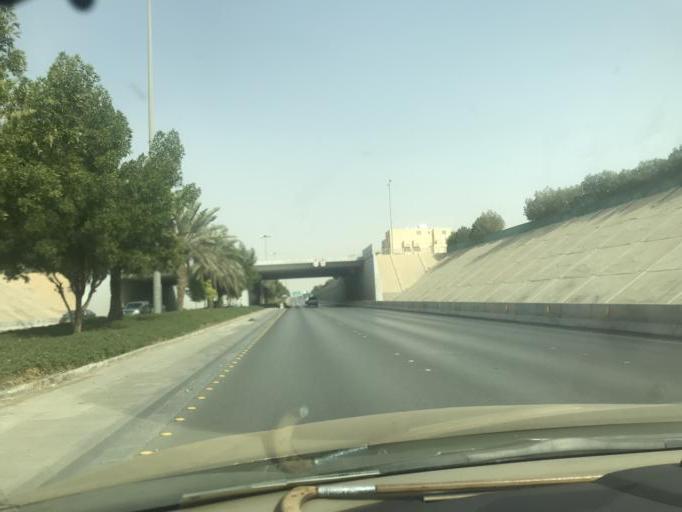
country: SA
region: Ar Riyad
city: Riyadh
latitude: 24.6673
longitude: 46.7955
